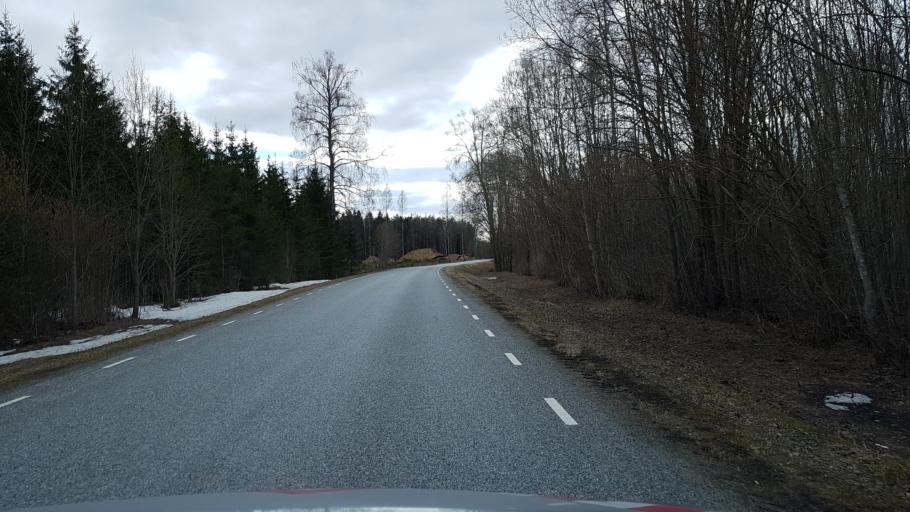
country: EE
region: Laeaene-Virumaa
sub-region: Tamsalu vald
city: Tamsalu
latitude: 59.2226
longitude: 26.1626
